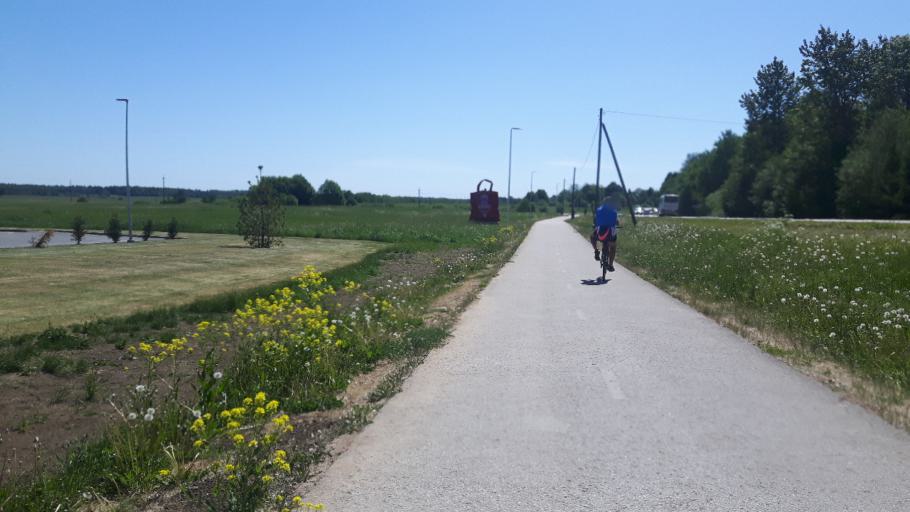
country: EE
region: Harju
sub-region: Saku vald
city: Saku
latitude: 59.2914
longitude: 24.6596
